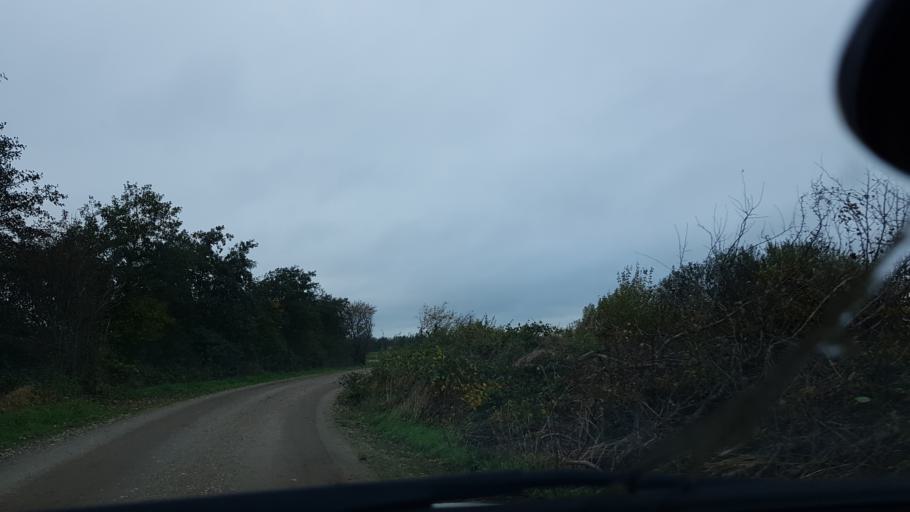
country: DK
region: South Denmark
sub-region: Esbjerg Kommune
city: Ribe
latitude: 55.2804
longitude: 8.8490
